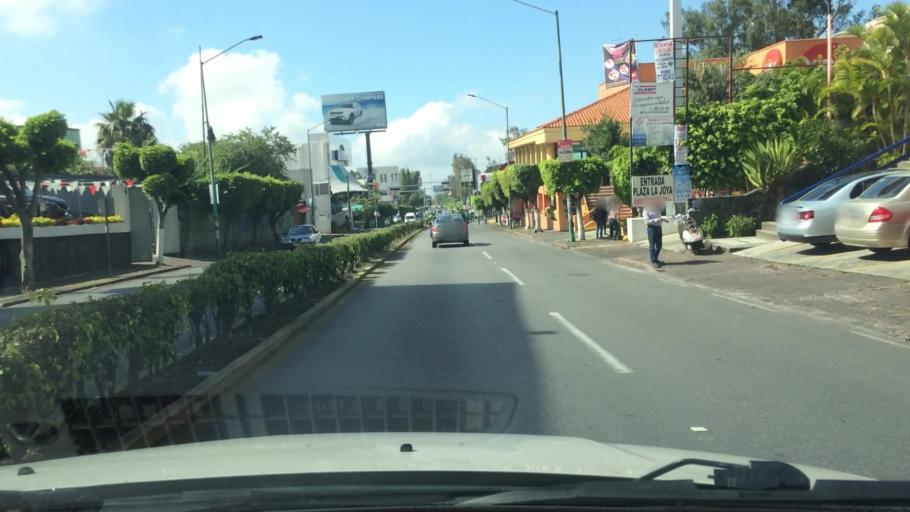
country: MX
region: Morelos
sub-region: Cuernavaca
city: Fraccionamiento Lomas de Ahuatlan
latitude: 18.9576
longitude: -99.2458
